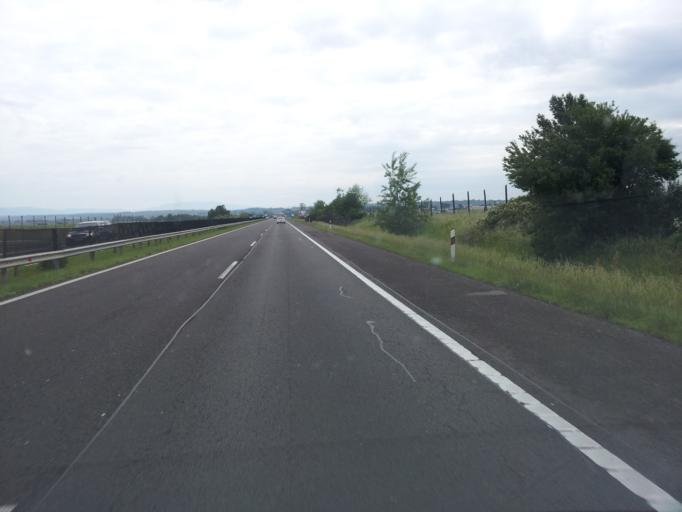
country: HU
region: Heves
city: Hered
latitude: 47.6726
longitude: 19.6372
